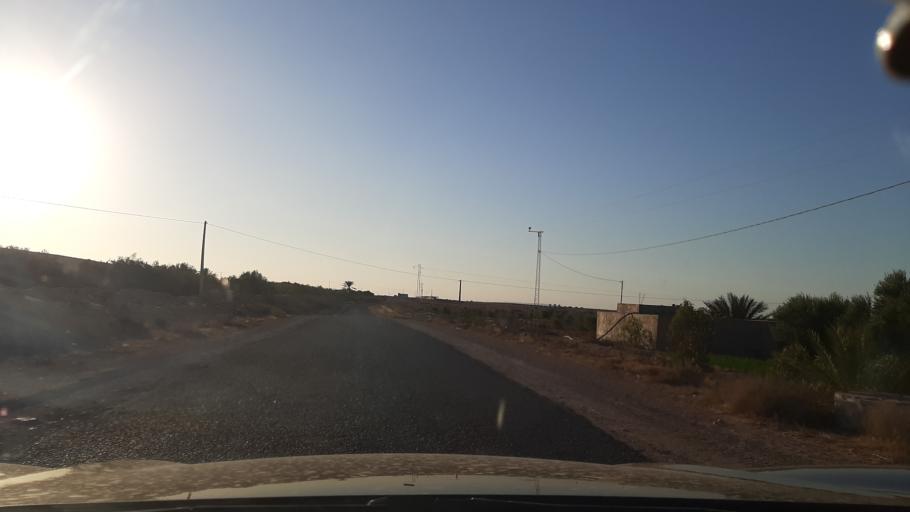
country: TN
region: Qabis
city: Matmata
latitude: 33.6189
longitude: 10.1460
